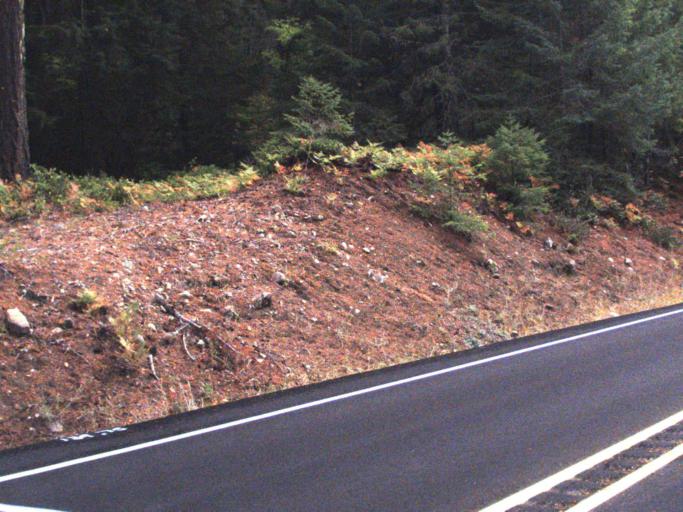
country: US
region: Washington
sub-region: Pierce County
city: Buckley
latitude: 46.6961
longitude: -121.5657
